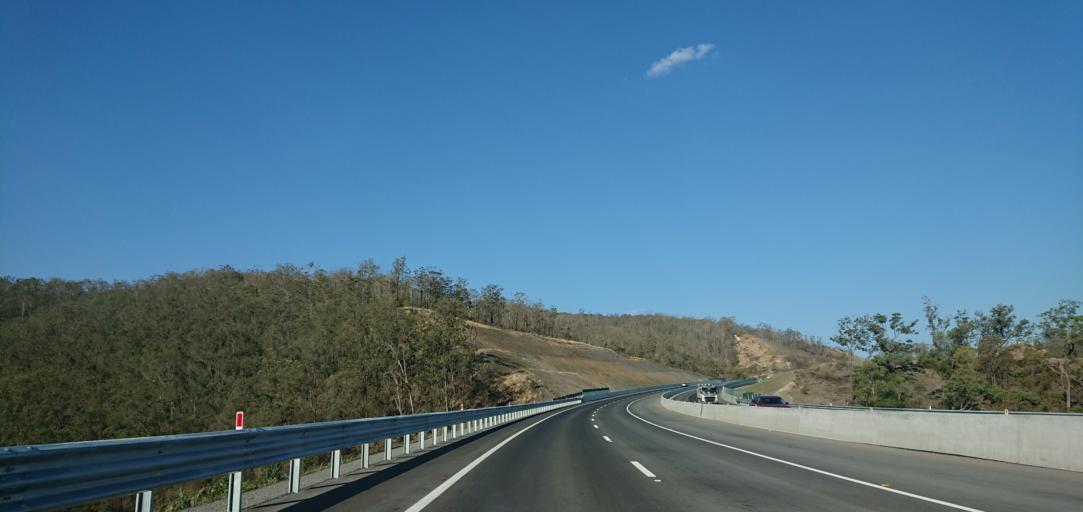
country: AU
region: Queensland
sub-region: Toowoomba
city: Wilsonton Heights
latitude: -27.4983
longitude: 151.9800
